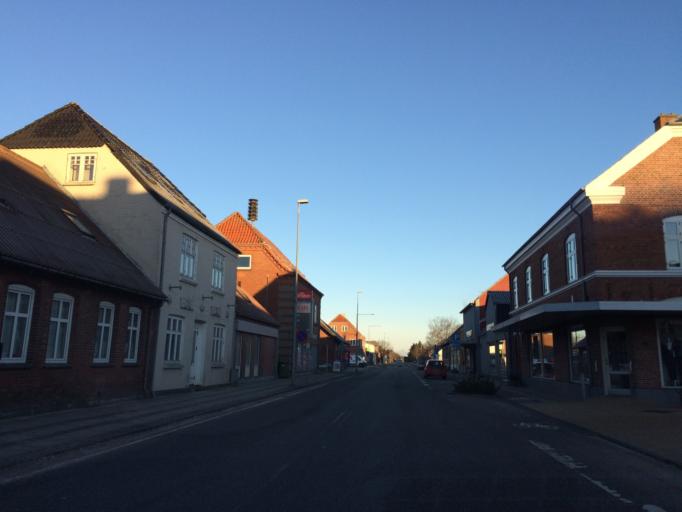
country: DK
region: Central Jutland
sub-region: Holstebro Kommune
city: Ulfborg
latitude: 56.3437
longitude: 8.3435
